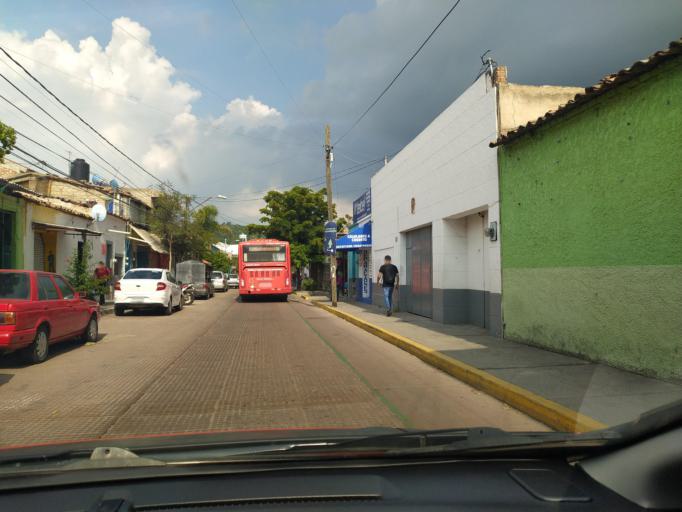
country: MX
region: Jalisco
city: Tlajomulco de Zuniga
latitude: 20.4765
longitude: -103.4495
